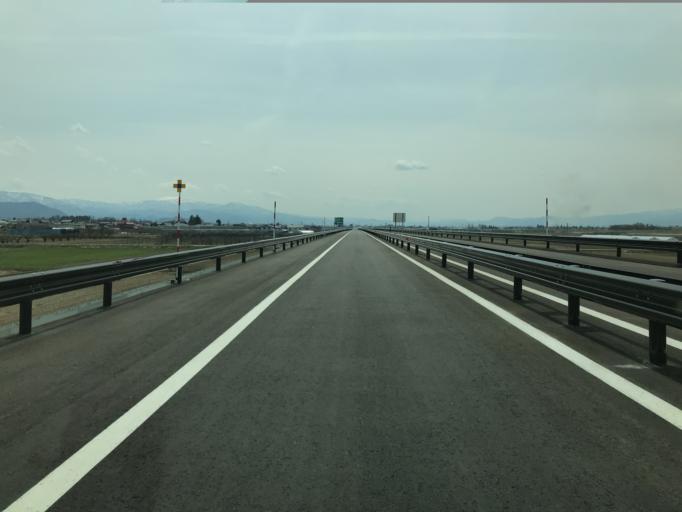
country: JP
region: Yamagata
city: Higashine
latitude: 38.4364
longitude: 140.3536
